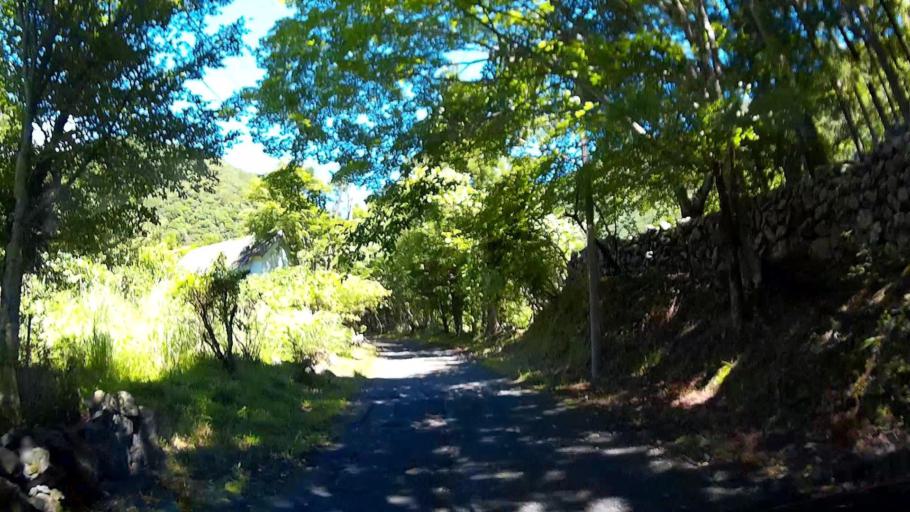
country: JP
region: Shizuoka
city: Fujinomiya
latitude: 35.2848
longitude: 138.3196
